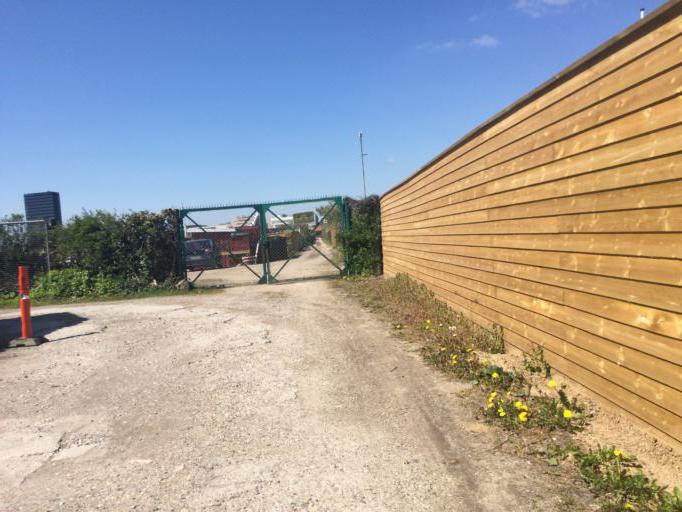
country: DK
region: Capital Region
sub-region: Tarnby Kommune
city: Tarnby
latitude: 55.6310
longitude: 12.5925
